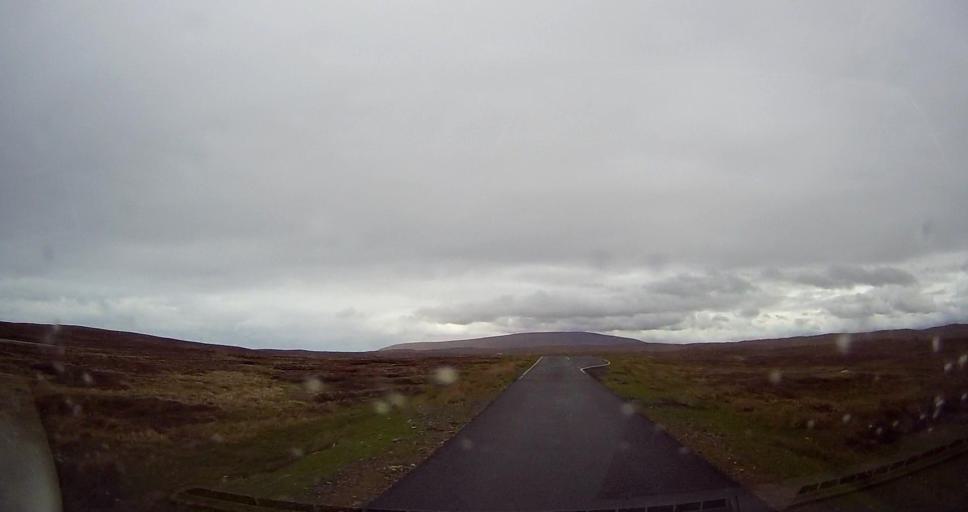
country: GB
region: Scotland
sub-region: Shetland Islands
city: Lerwick
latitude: 60.4896
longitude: -1.5872
